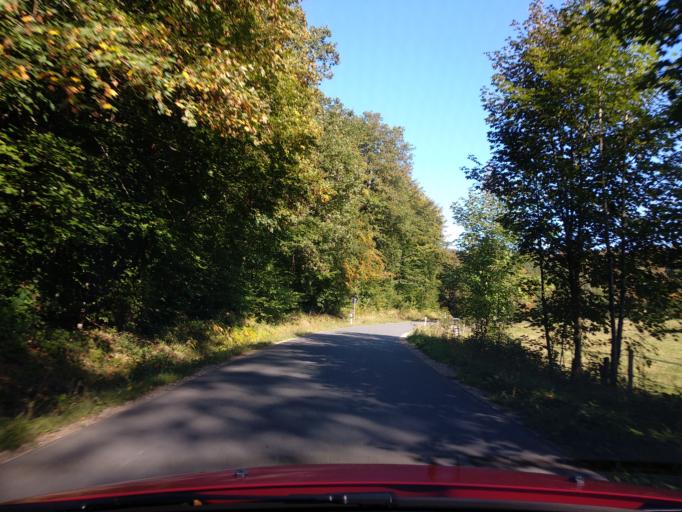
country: DE
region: Lower Saxony
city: Derental
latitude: 51.6908
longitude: 9.4516
